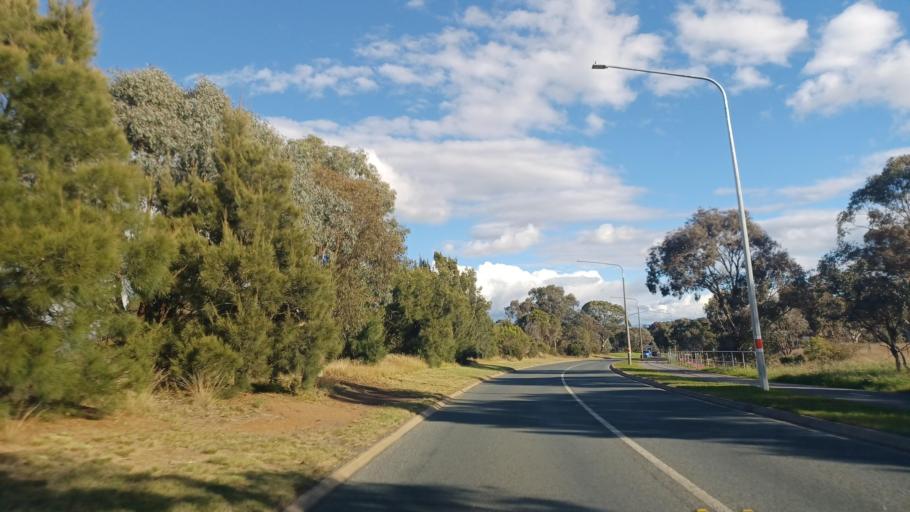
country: AU
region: Australian Capital Territory
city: Belconnen
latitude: -35.1907
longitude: 149.0711
